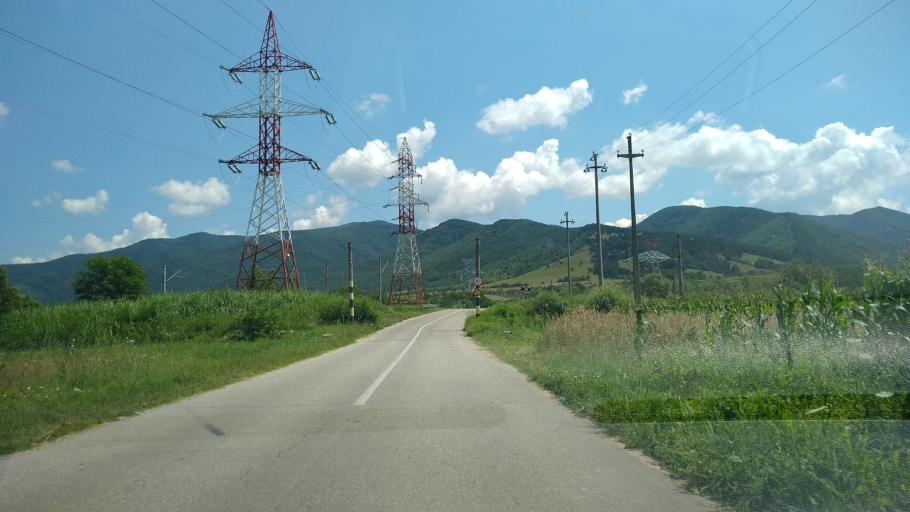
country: RO
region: Hunedoara
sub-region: Comuna Santamaria-Orlea
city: Santamaria-Orlea
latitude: 45.5894
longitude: 22.9868
